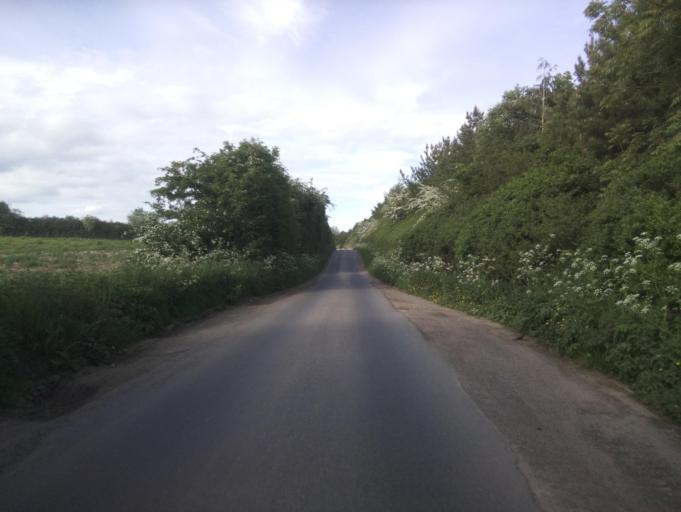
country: GB
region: England
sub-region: Gloucestershire
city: Westfield
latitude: 51.9284
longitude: -1.8327
